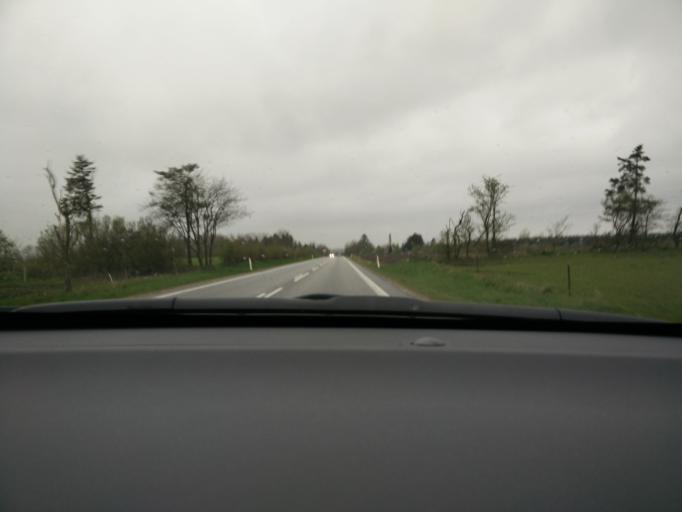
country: DK
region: Central Jutland
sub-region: Viborg Kommune
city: Stoholm
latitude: 56.5138
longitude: 9.2781
